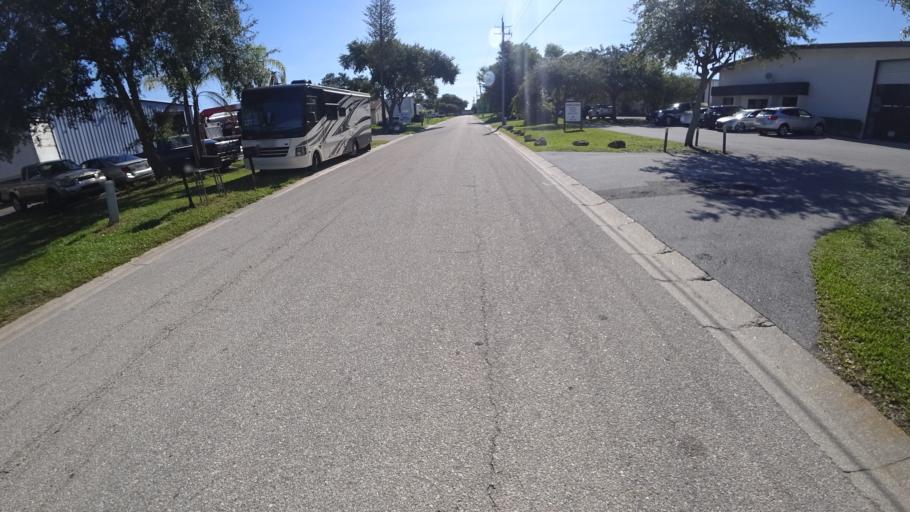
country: US
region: Florida
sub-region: Manatee County
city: Whitfield
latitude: 27.4201
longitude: -82.5388
